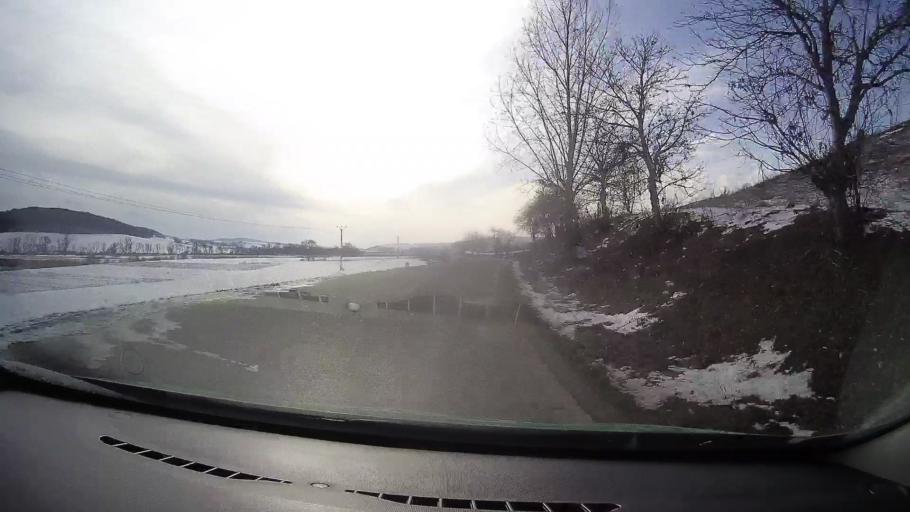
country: RO
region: Sibiu
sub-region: Comuna Iacobeni
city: Iacobeni
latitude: 46.0375
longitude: 24.7268
